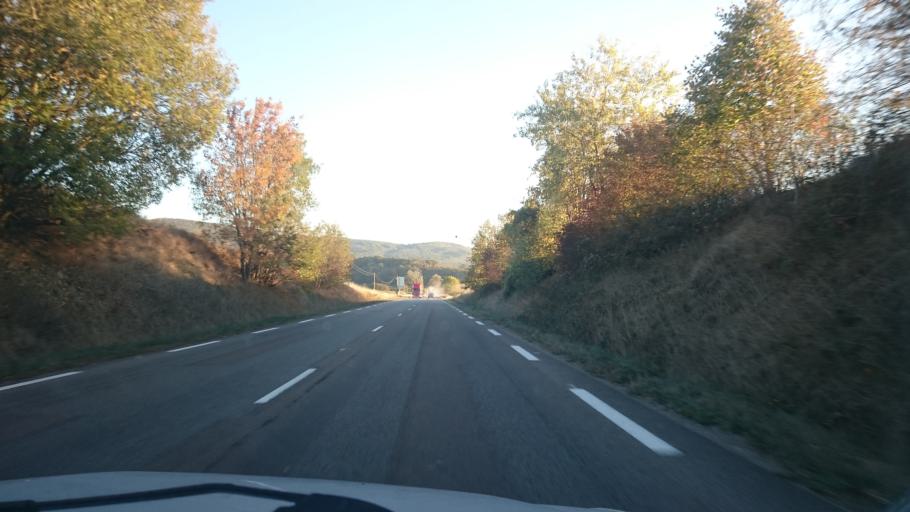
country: FR
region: Franche-Comte
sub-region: Departement du Doubs
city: Quingey
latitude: 47.0653
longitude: 5.8819
